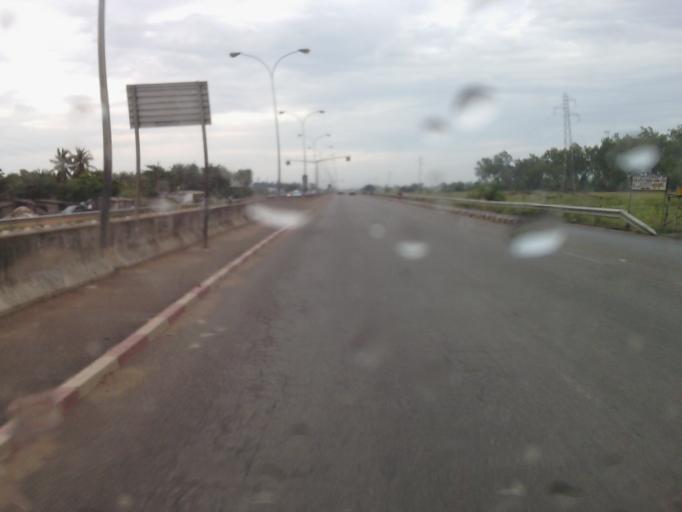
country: BJ
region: Queme
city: Porto-Novo
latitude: 6.3748
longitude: 2.5647
